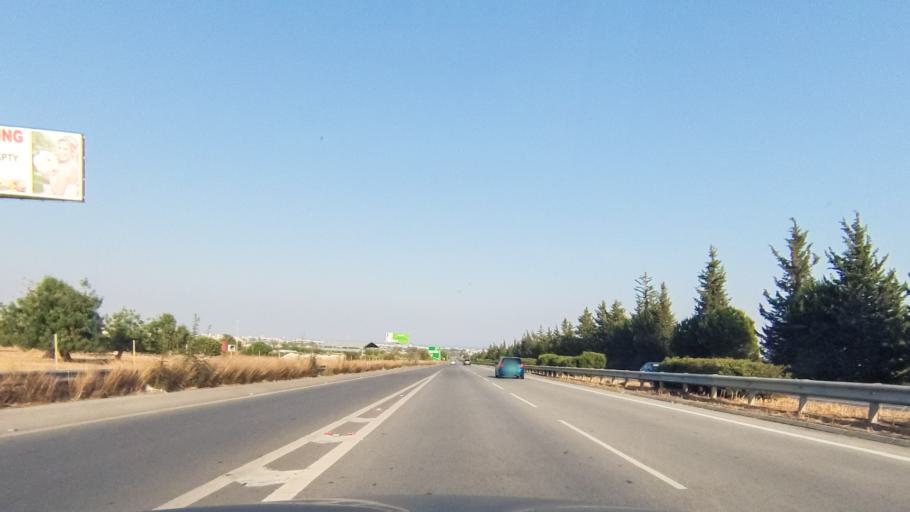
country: CY
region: Limassol
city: Ypsonas
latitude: 34.6940
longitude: 32.9705
